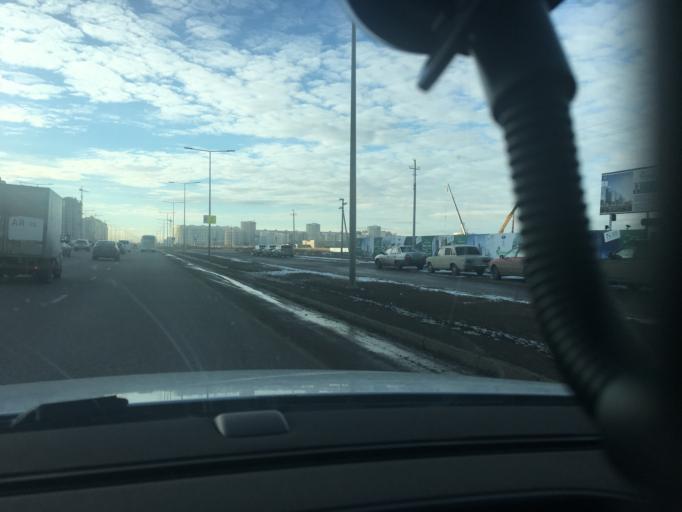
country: KZ
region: Astana Qalasy
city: Astana
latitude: 51.1298
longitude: 71.3840
